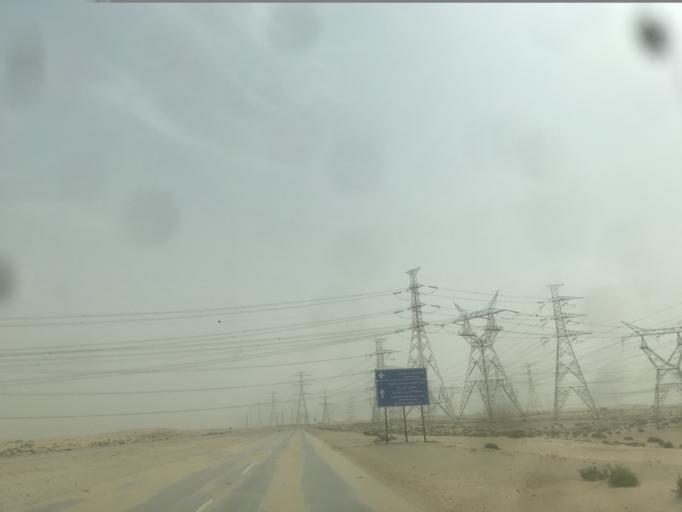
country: SA
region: Eastern Province
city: Abqaiq
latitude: 25.9067
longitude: 49.9074
